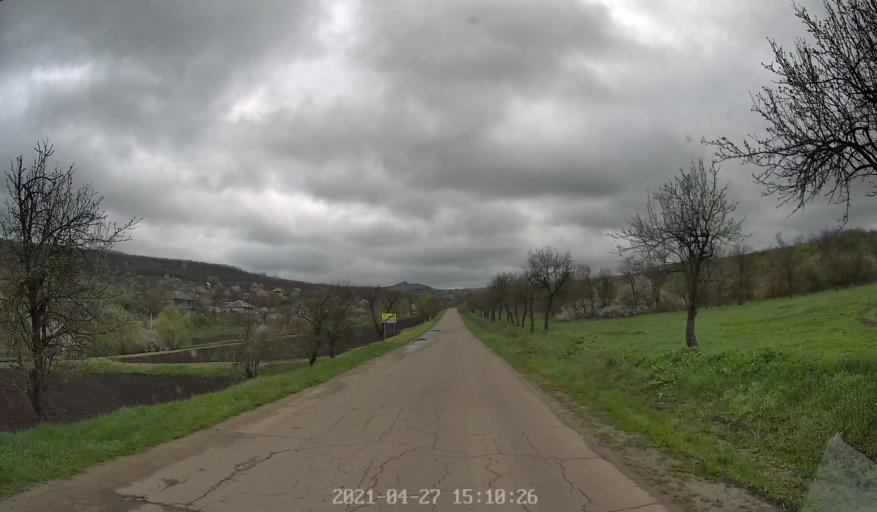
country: MD
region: Chisinau
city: Vadul lui Voda
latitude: 47.0406
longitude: 29.0328
